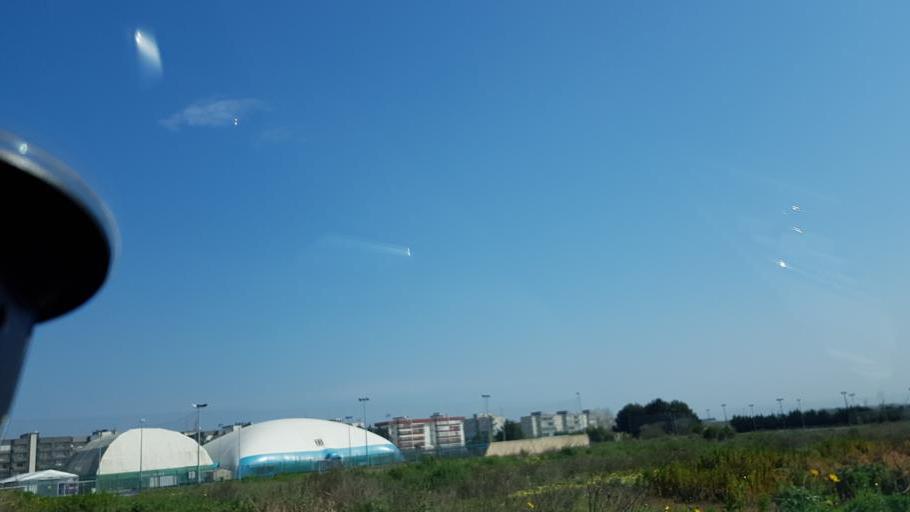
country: IT
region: Apulia
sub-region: Provincia di Brindisi
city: Brindisi
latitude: 40.6148
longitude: 17.9310
